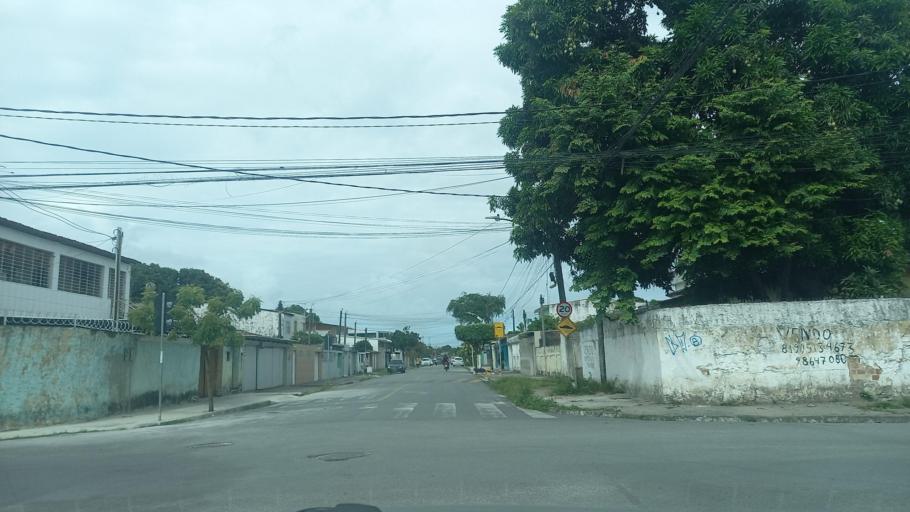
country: BR
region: Pernambuco
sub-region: Recife
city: Recife
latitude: -8.1104
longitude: -34.9206
